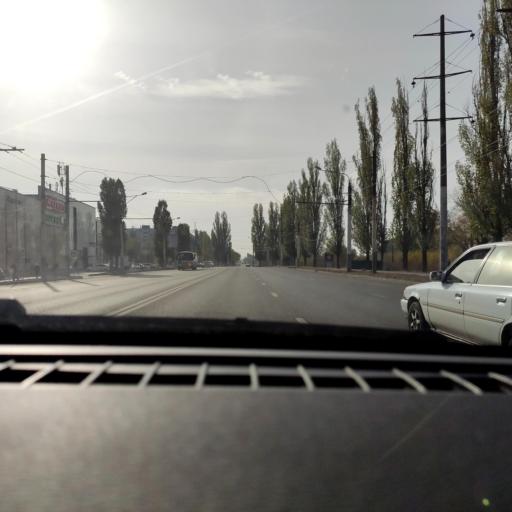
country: RU
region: Voronezj
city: Maslovka
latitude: 51.6043
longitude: 39.2370
